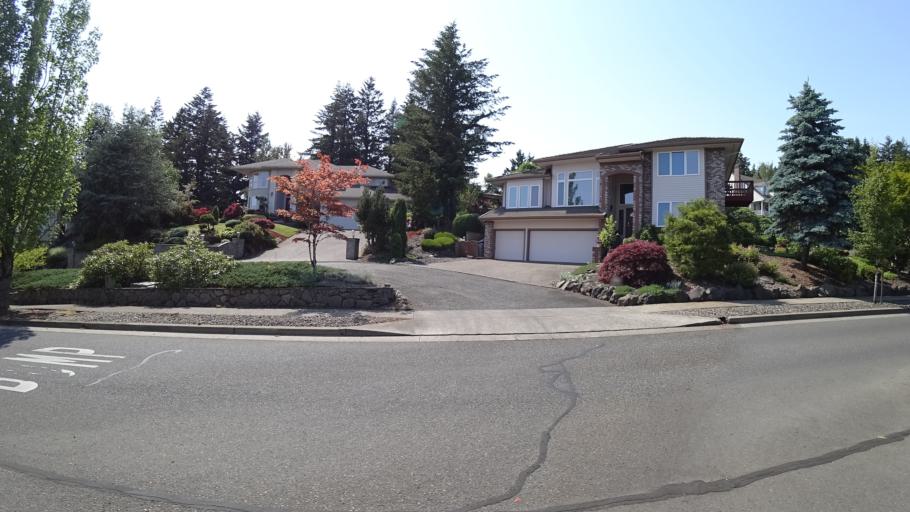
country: US
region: Oregon
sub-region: Clackamas County
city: Happy Valley
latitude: 45.4407
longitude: -122.5422
